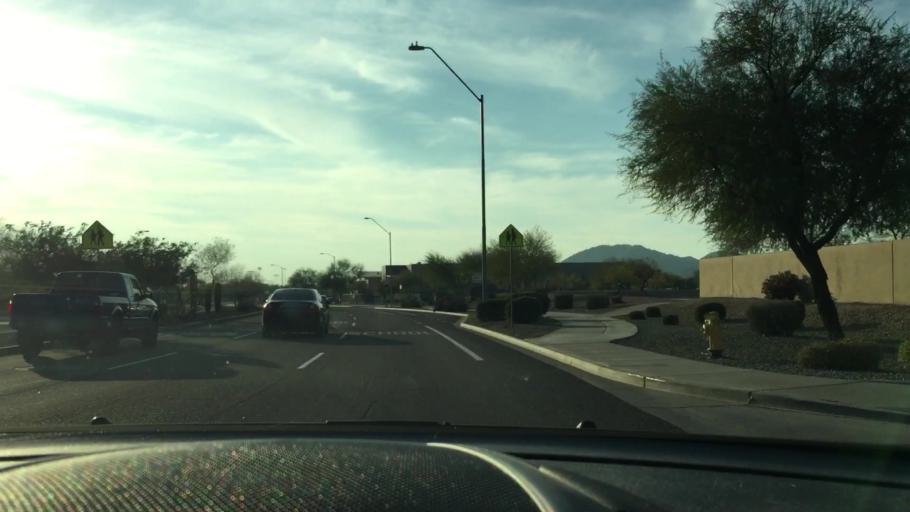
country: US
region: Arizona
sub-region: Maricopa County
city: Sun City
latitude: 33.7123
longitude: -112.2059
